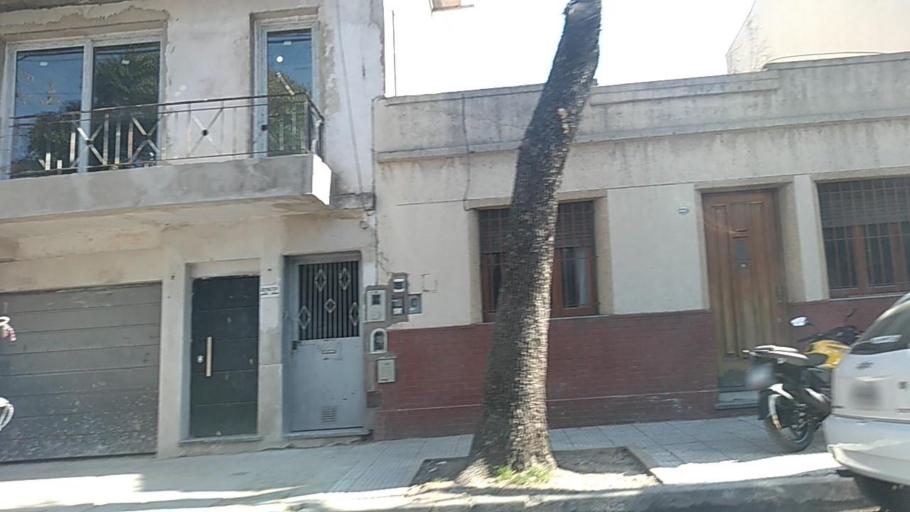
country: AR
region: Buenos Aires F.D.
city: Villa Santa Rita
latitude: -34.6112
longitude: -58.4936
